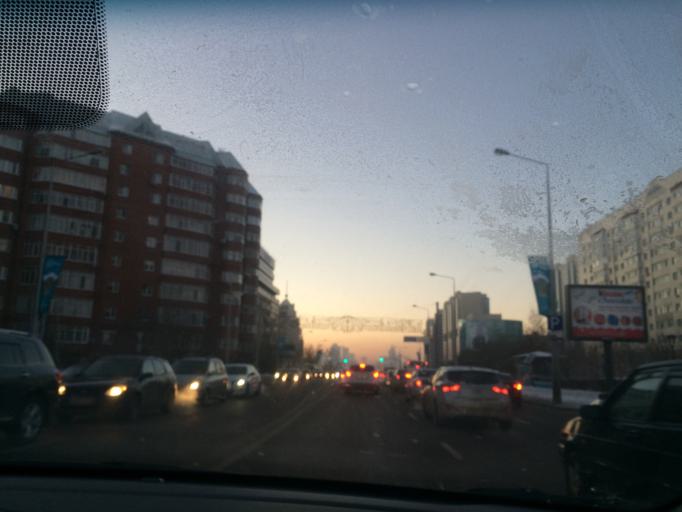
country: KZ
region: Astana Qalasy
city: Astana
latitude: 51.1651
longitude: 71.4091
